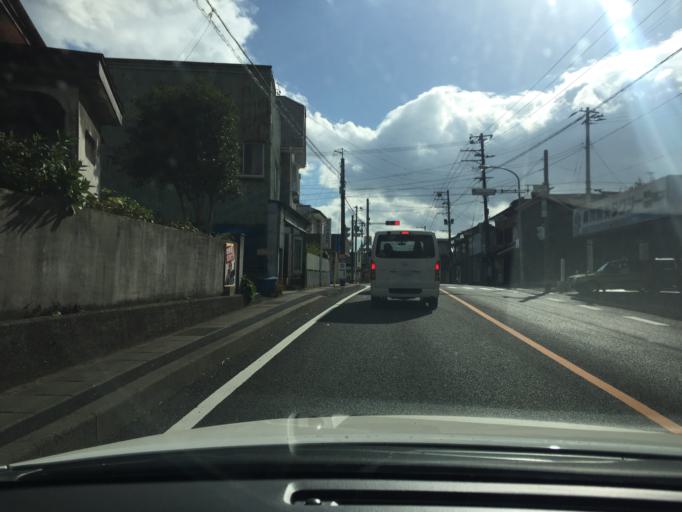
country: JP
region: Fukushima
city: Nihommatsu
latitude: 37.6603
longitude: 140.4618
